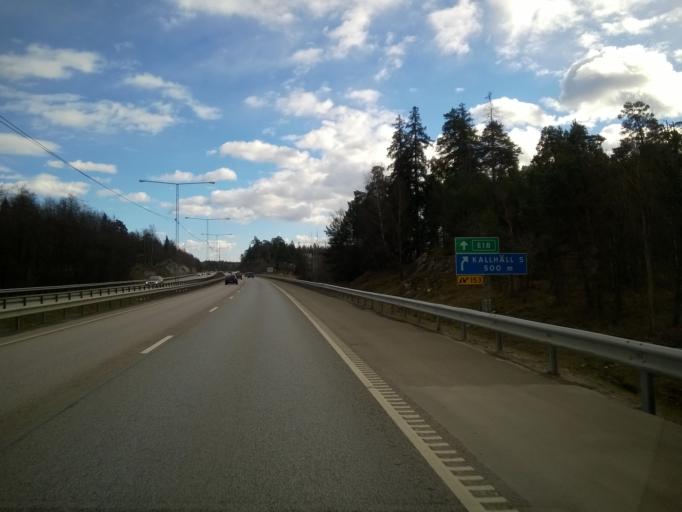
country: SE
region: Stockholm
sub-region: Jarfalla Kommun
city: Jakobsberg
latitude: 59.4563
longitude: 17.8294
